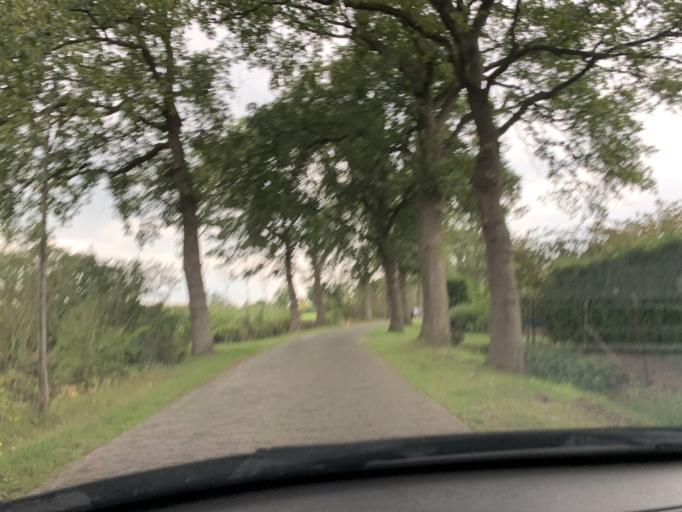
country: DE
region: Lower Saxony
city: Westerstede
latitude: 53.2430
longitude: 7.8939
